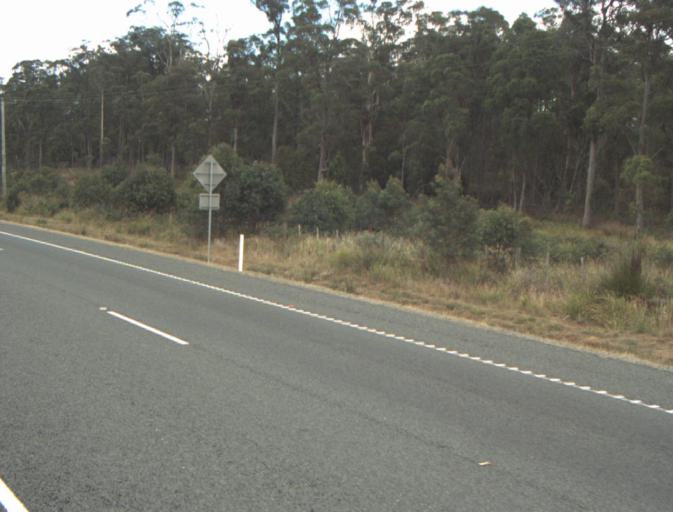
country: AU
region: Tasmania
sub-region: Launceston
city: Mayfield
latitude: -41.2571
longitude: 147.0253
